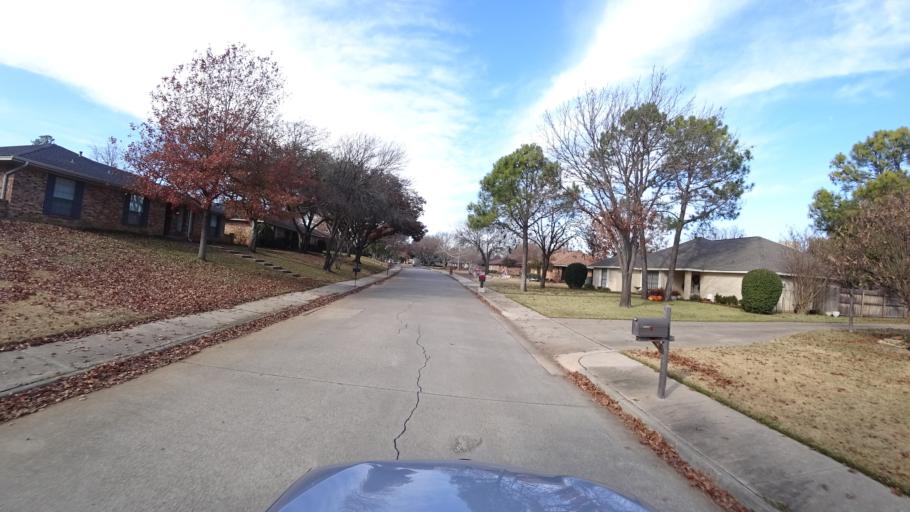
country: US
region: Texas
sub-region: Denton County
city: Lewisville
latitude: 33.0525
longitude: -97.0301
